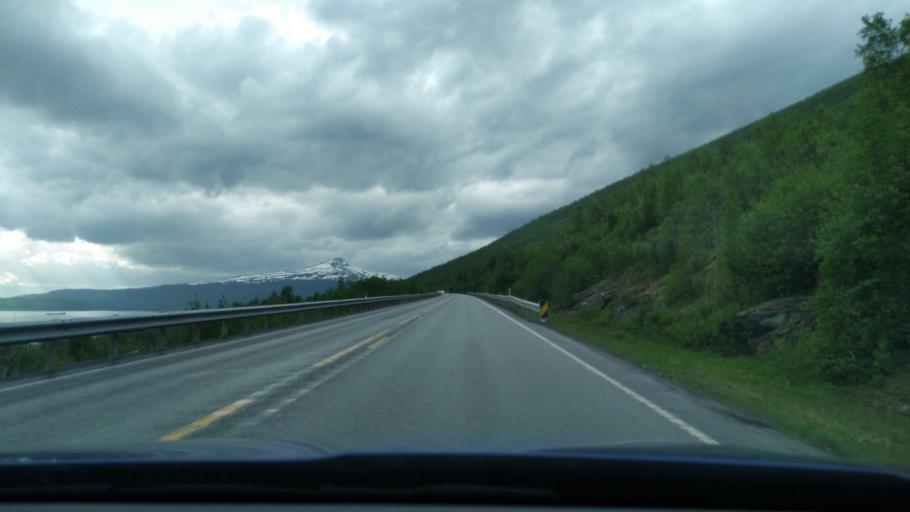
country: NO
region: Troms
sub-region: Balsfjord
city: Storsteinnes
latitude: 69.2326
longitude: 19.4831
